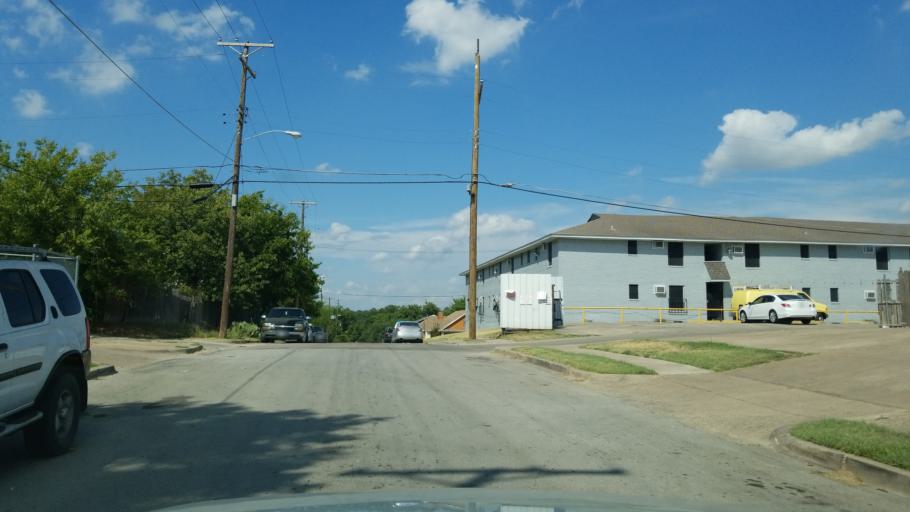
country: US
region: Texas
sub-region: Dallas County
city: Dallas
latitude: 32.7548
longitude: -96.8131
